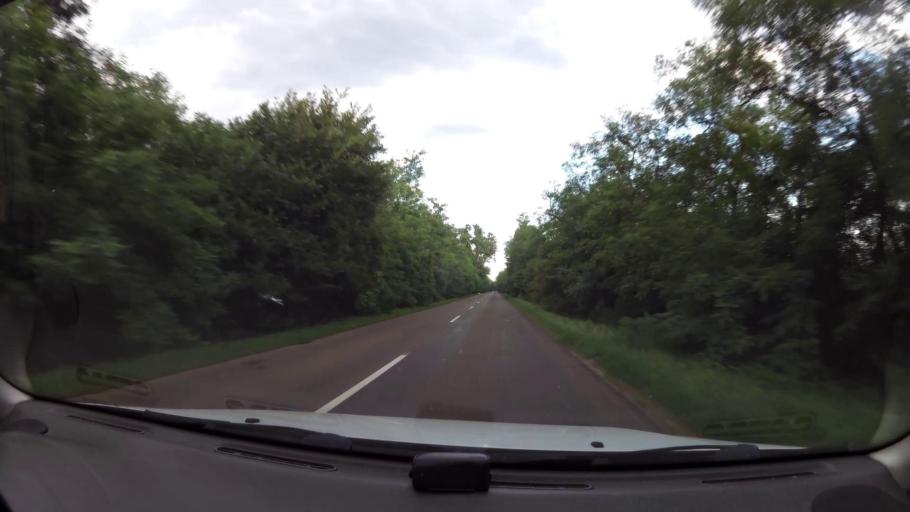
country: HU
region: Pest
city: Tapiosag
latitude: 47.3885
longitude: 19.6481
